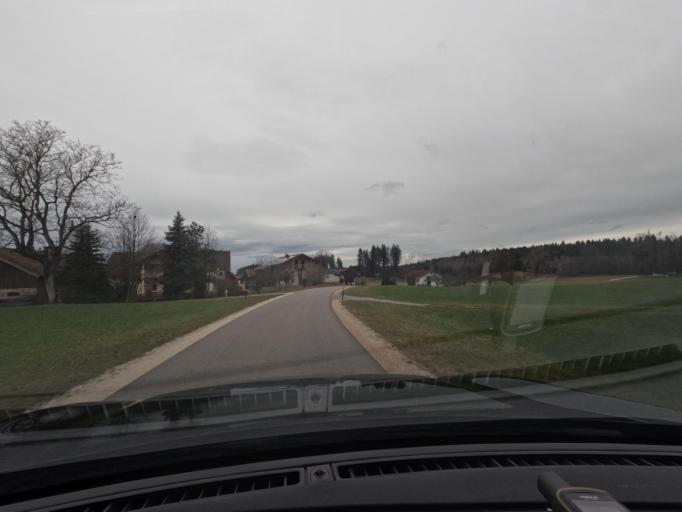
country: DE
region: Bavaria
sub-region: Upper Bavaria
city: Surberg
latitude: 47.8705
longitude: 12.6760
